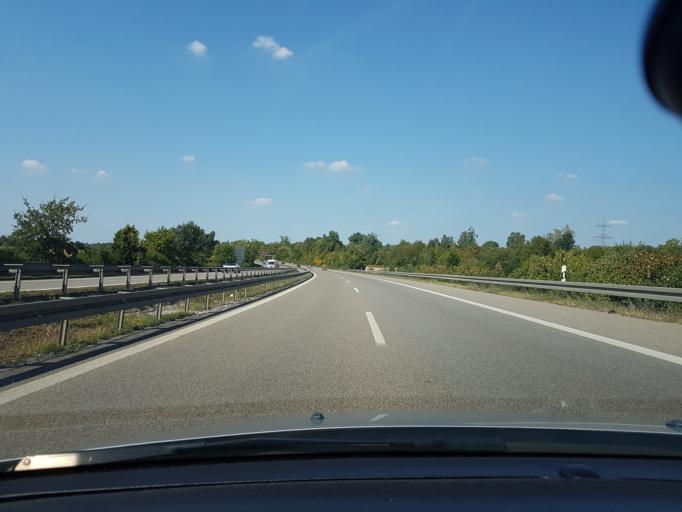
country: DE
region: Bavaria
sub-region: Swabia
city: Gersthofen
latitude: 48.4588
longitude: 10.8793
